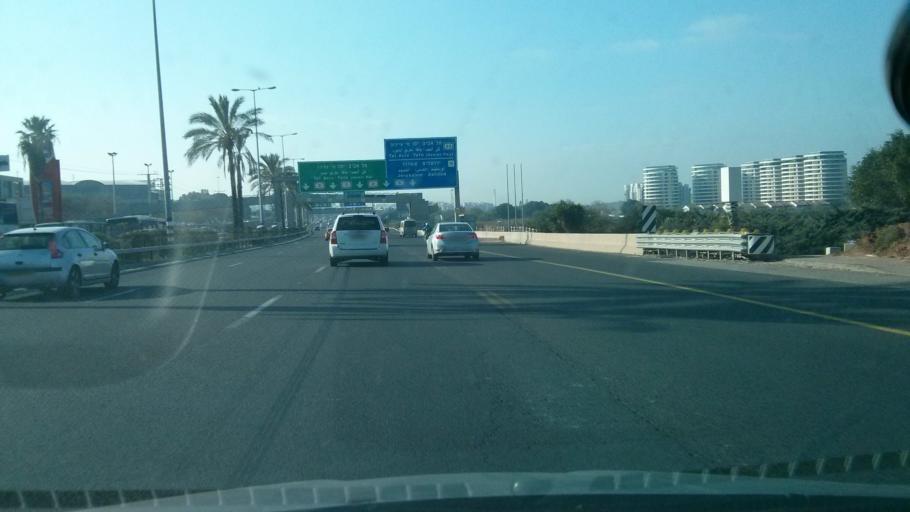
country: IL
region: Tel Aviv
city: Herzliya Pituah
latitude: 32.1485
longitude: 34.8038
